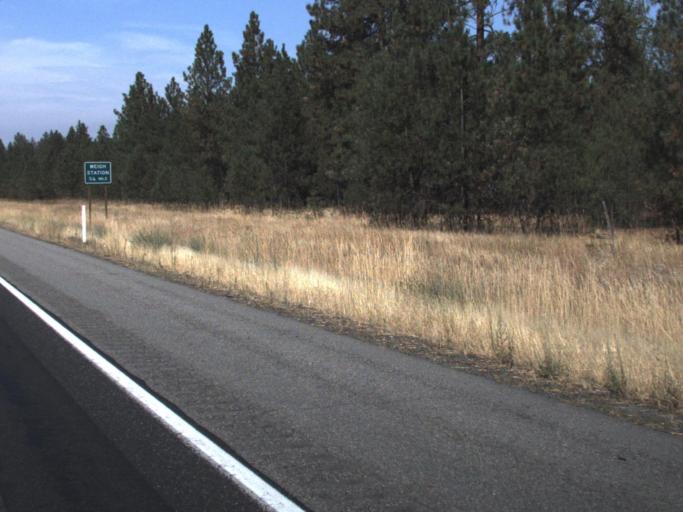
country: US
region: Washington
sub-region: Spokane County
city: Mead
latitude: 47.8512
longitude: -117.3549
